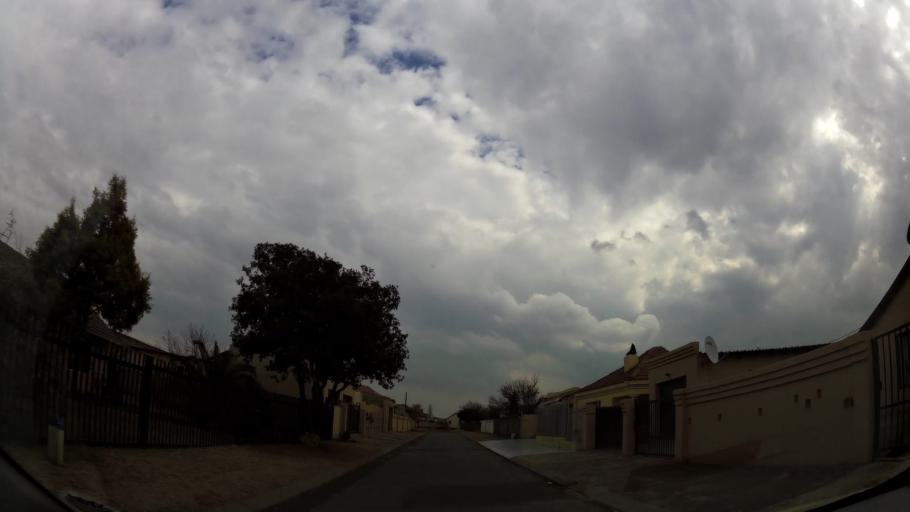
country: ZA
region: Gauteng
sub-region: Ekurhuleni Metropolitan Municipality
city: Germiston
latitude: -26.3842
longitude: 28.1600
